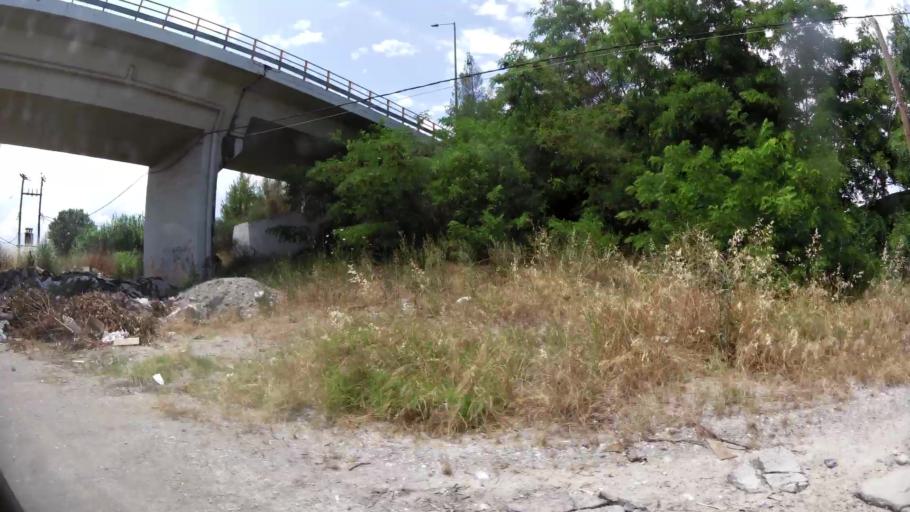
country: GR
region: Central Macedonia
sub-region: Nomos Pierias
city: Peristasi
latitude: 40.2633
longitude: 22.5304
